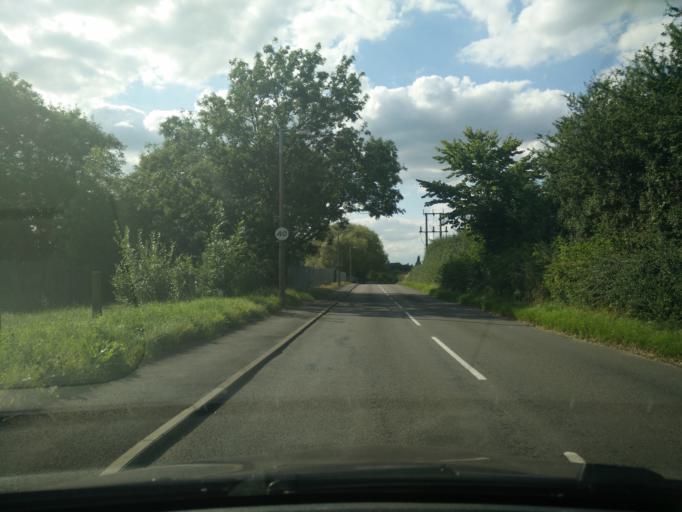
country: GB
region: England
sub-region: Derbyshire
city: Ilkeston
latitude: 52.9476
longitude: -1.3108
